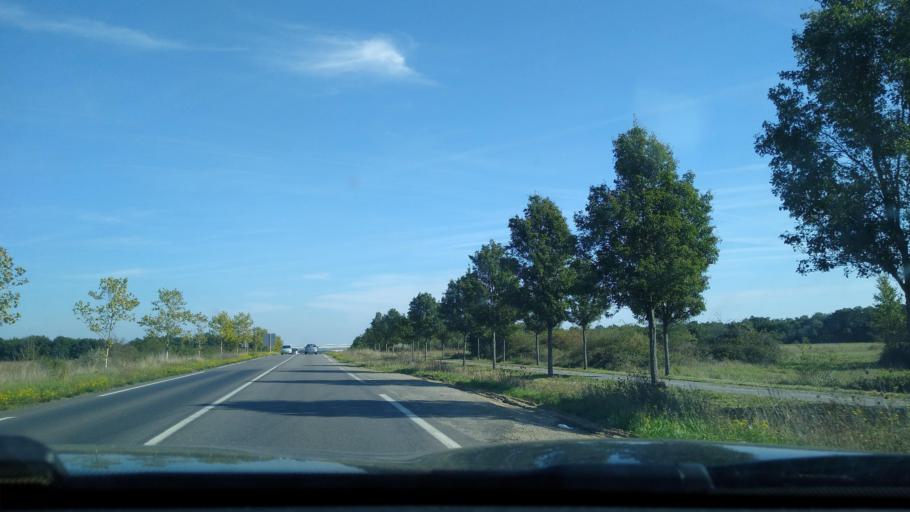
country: FR
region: Midi-Pyrenees
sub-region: Departement de la Haute-Garonne
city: Aussonne
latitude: 43.6660
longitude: 1.3104
